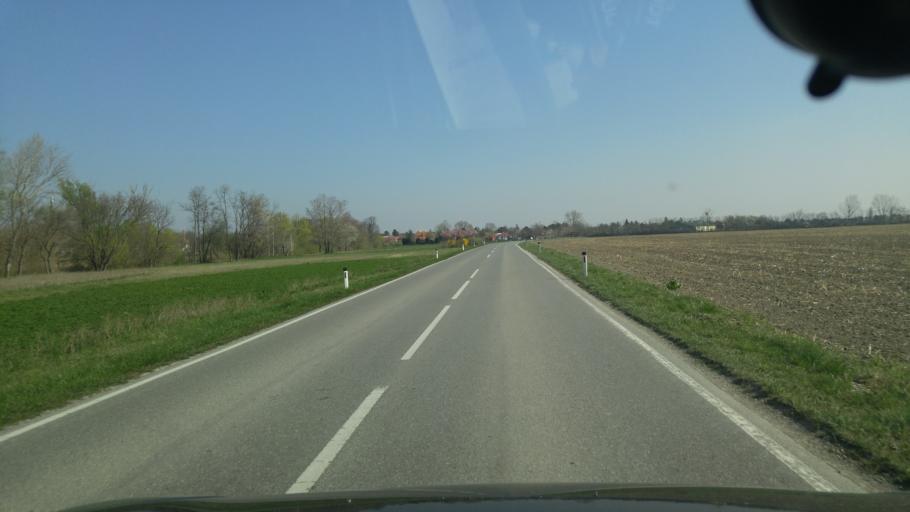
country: AT
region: Lower Austria
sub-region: Politischer Bezirk Baden
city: Trumau
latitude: 47.9864
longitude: 16.3376
